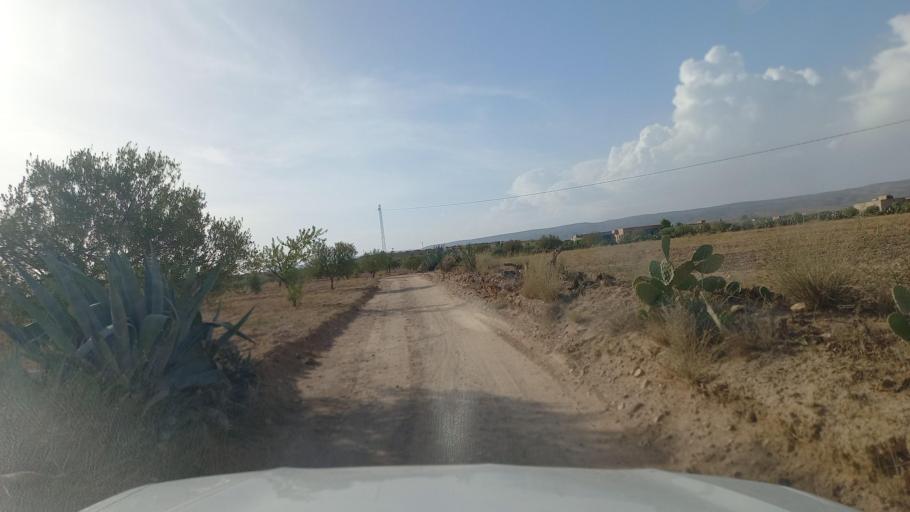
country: TN
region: Al Qasrayn
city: Kasserine
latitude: 35.2317
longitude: 8.9233
